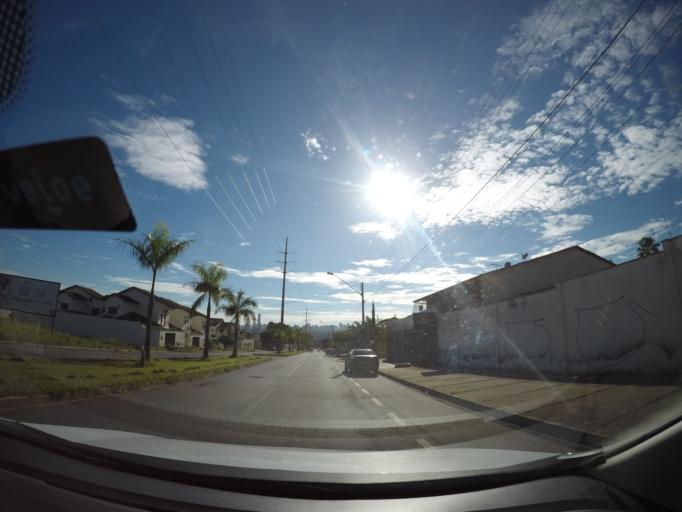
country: BR
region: Goias
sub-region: Goiania
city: Goiania
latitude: -16.7258
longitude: -49.3004
